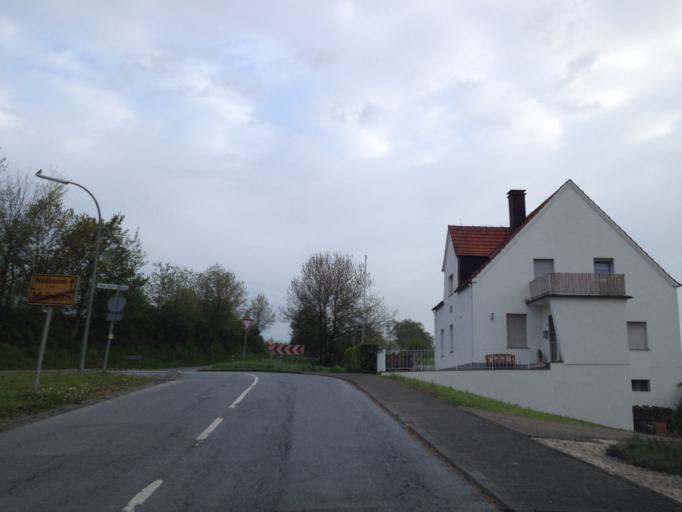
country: DE
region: North Rhine-Westphalia
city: Warstein
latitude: 51.4949
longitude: 8.2843
